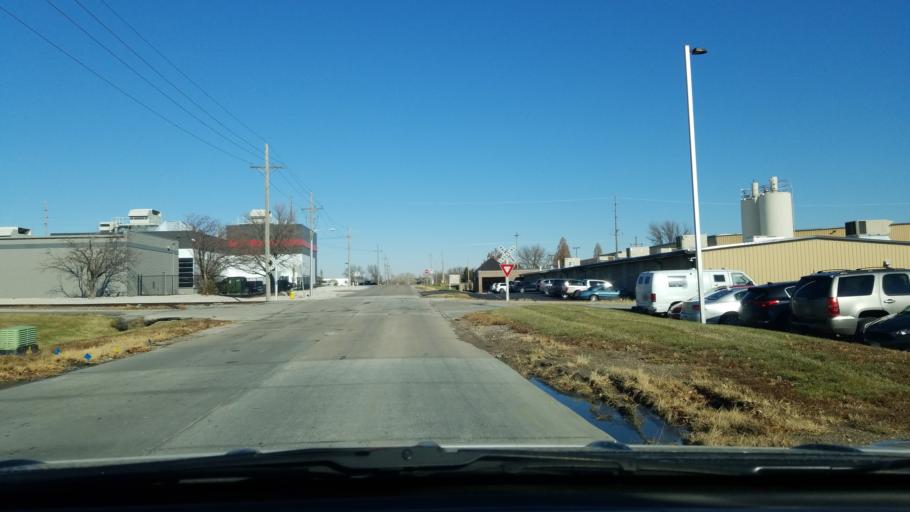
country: US
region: Nebraska
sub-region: Douglas County
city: Ralston
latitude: 41.2148
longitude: -96.0719
